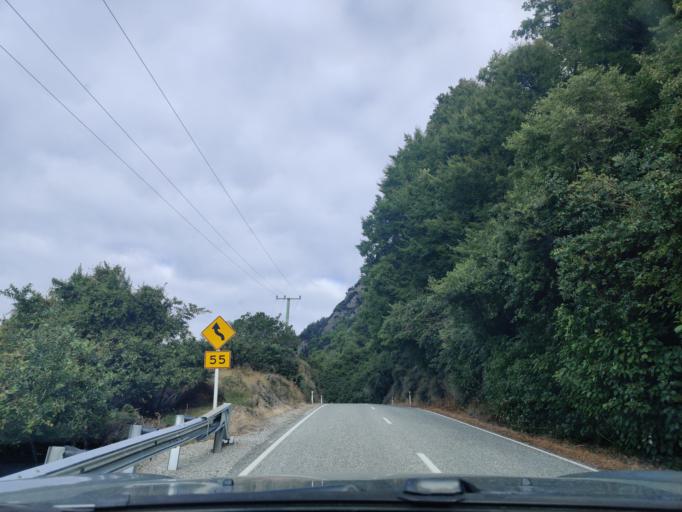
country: NZ
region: Otago
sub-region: Queenstown-Lakes District
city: Queenstown
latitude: -45.0755
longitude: 168.4928
